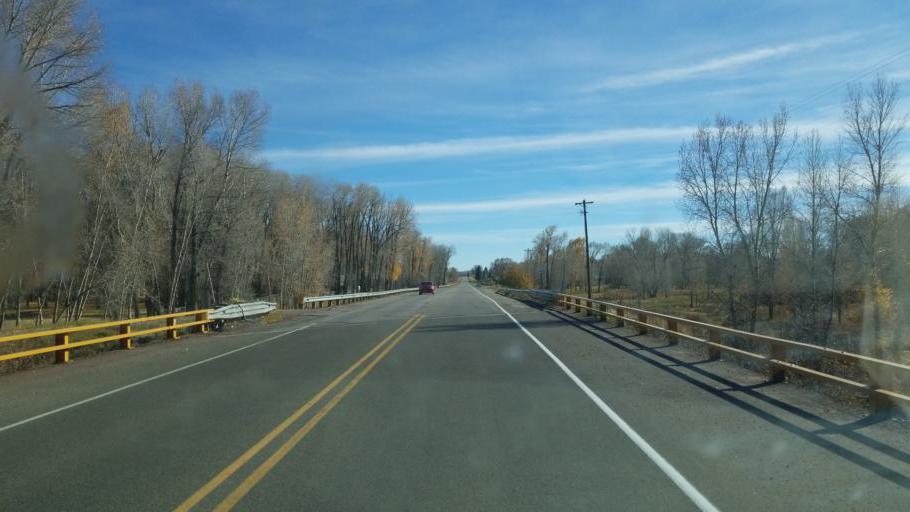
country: US
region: New Mexico
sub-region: Rio Arriba County
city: Chama
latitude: 36.8782
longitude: -106.5837
